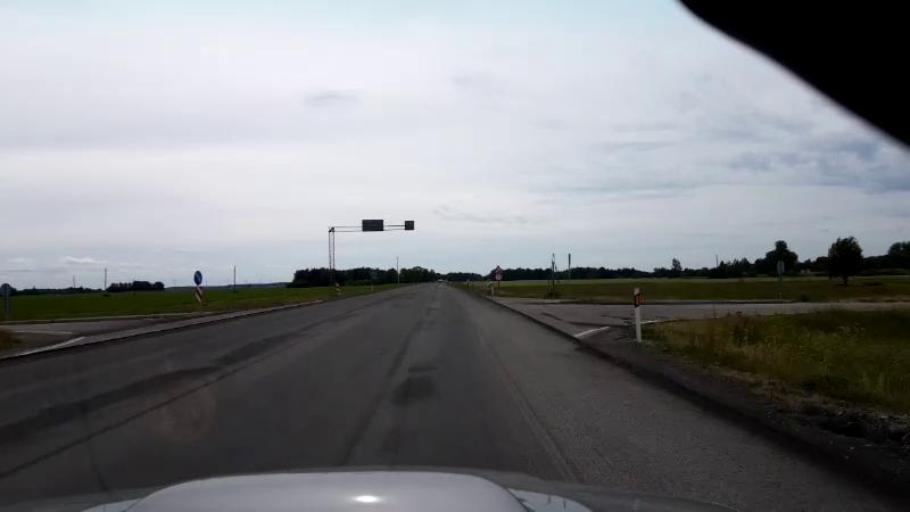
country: LV
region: Bauskas Rajons
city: Bauska
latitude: 56.3047
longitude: 24.3410
